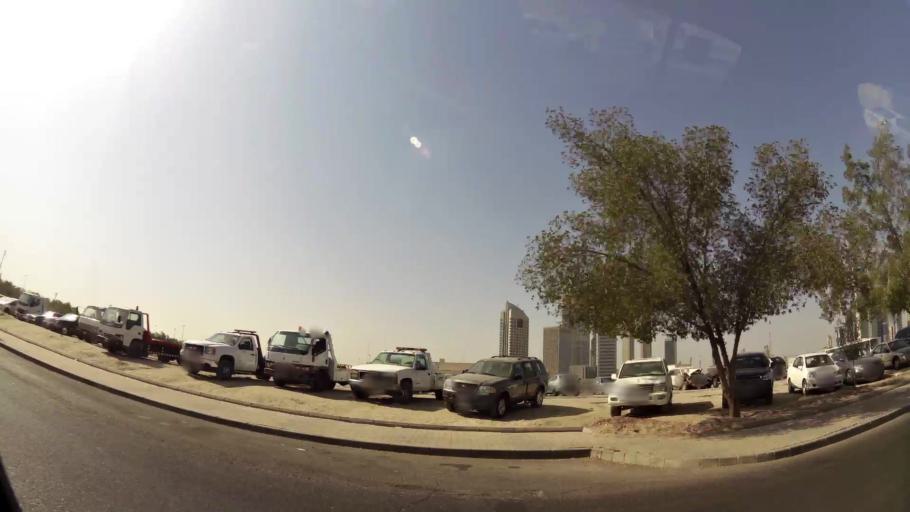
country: KW
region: Al Asimah
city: Kuwait City
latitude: 29.3672
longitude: 47.9891
